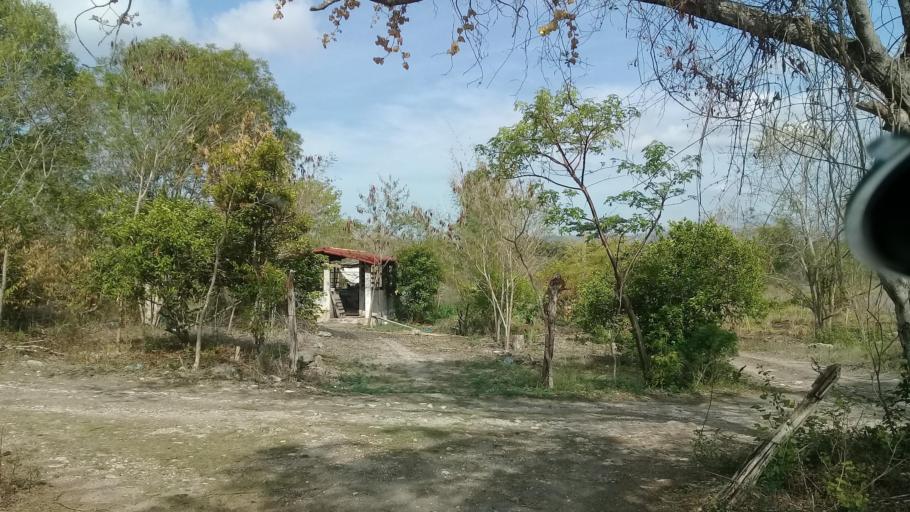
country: MX
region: Veracruz
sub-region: Emiliano Zapata
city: Plan del Rio
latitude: 19.3864
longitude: -96.6422
